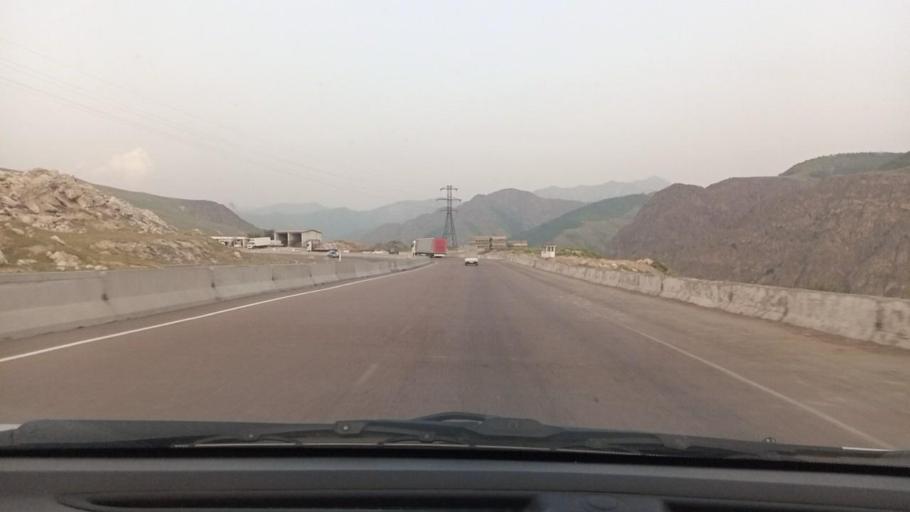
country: UZ
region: Toshkent
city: Angren
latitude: 41.0711
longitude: 70.2485
